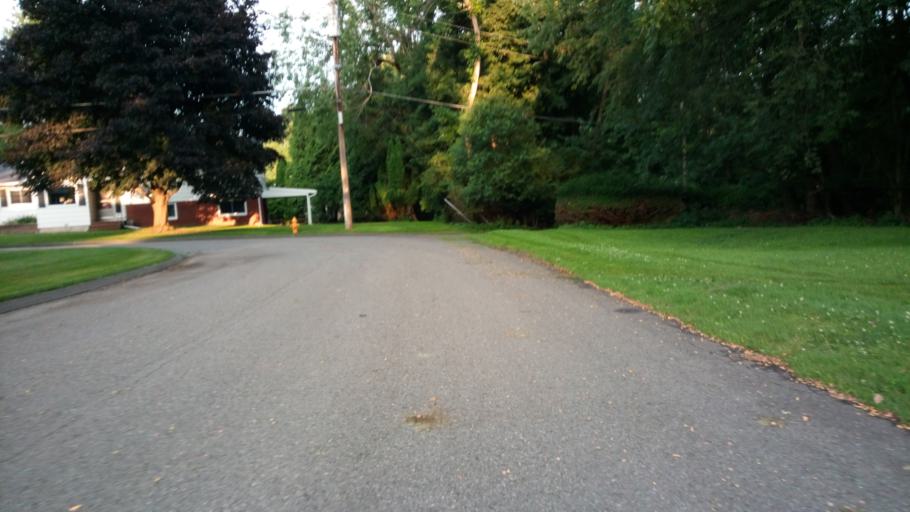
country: US
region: New York
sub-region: Chemung County
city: West Elmira
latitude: 42.0756
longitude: -76.8517
